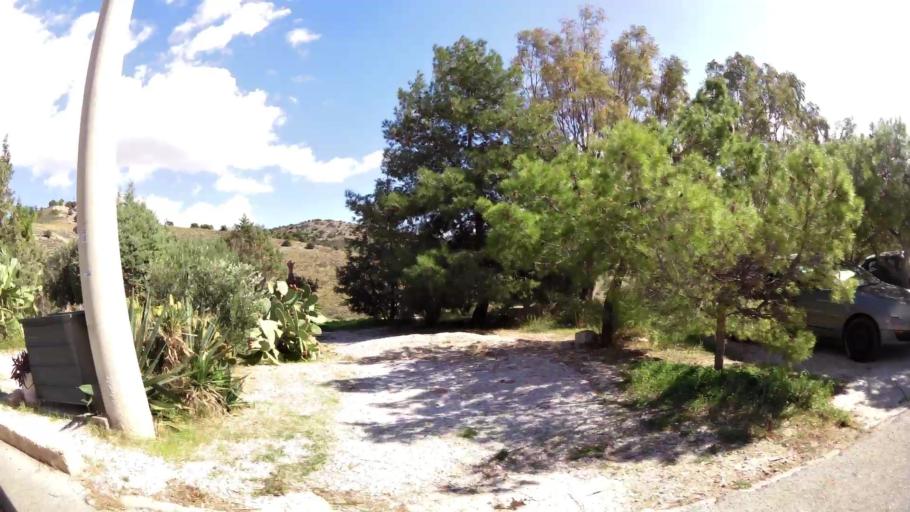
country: GR
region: Attica
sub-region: Nomarchia Anatolikis Attikis
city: Voula
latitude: 37.8475
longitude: 23.7850
